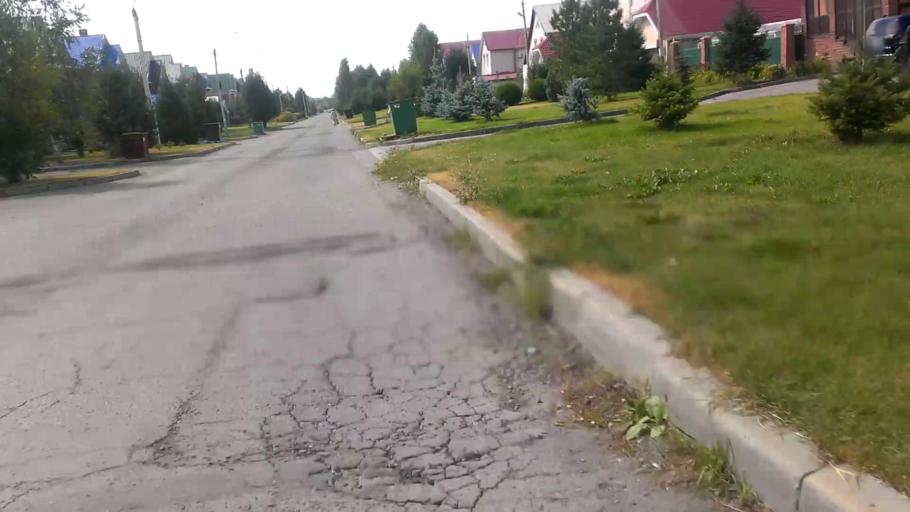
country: RU
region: Altai Krai
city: Novosilikatnyy
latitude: 53.3570
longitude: 83.6548
